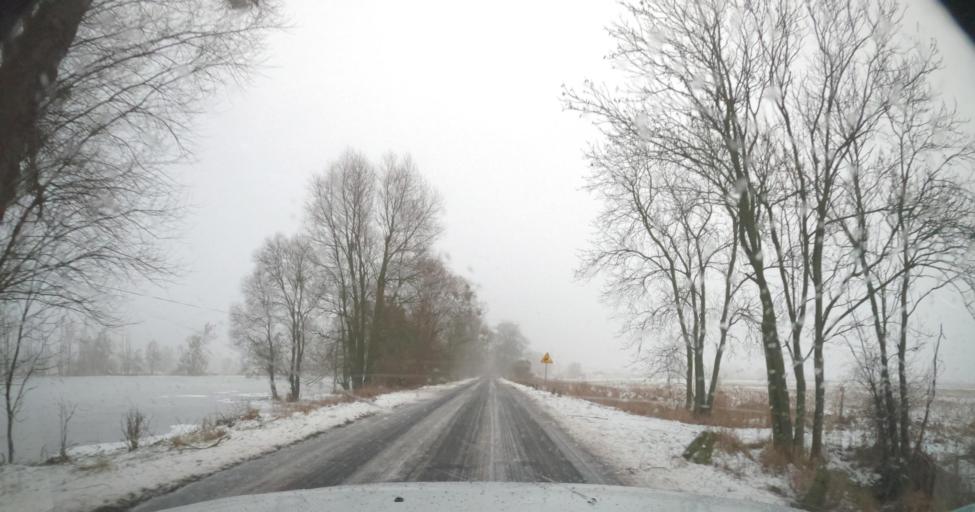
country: PL
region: West Pomeranian Voivodeship
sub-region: Powiat goleniowski
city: Stepnica
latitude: 53.5719
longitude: 14.6906
